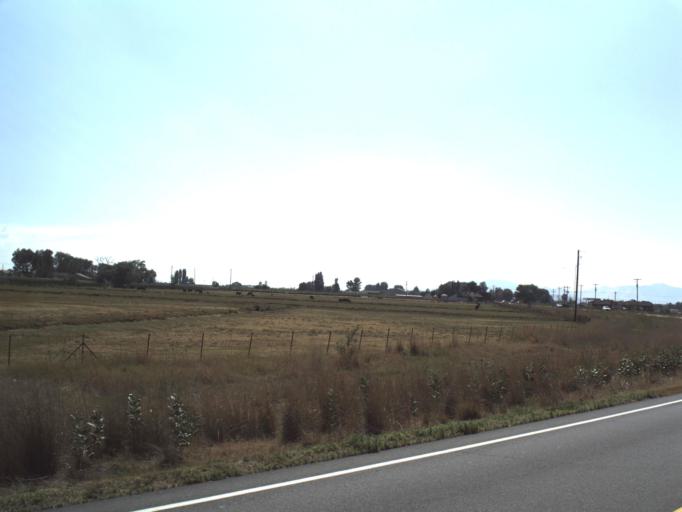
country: US
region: Utah
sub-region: Weber County
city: West Haven
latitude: 41.2444
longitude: -112.0831
